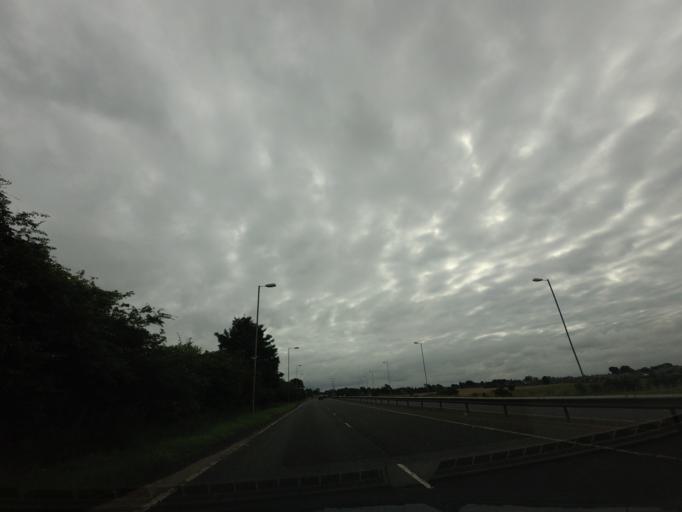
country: GB
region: Scotland
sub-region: Dumfries and Galloway
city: Gretna
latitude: 54.9999
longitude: -3.0719
